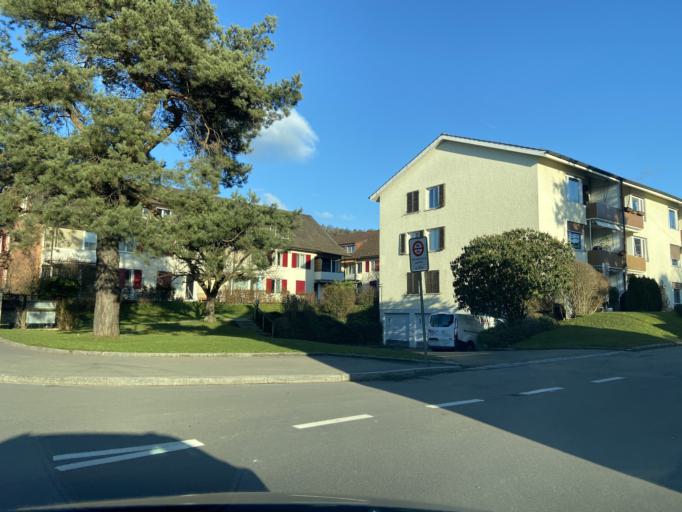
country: CH
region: Zurich
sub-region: Bezirk Winterthur
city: Wuelflingen (Kreis 6) / Lindenplatz
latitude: 47.5120
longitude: 8.6940
